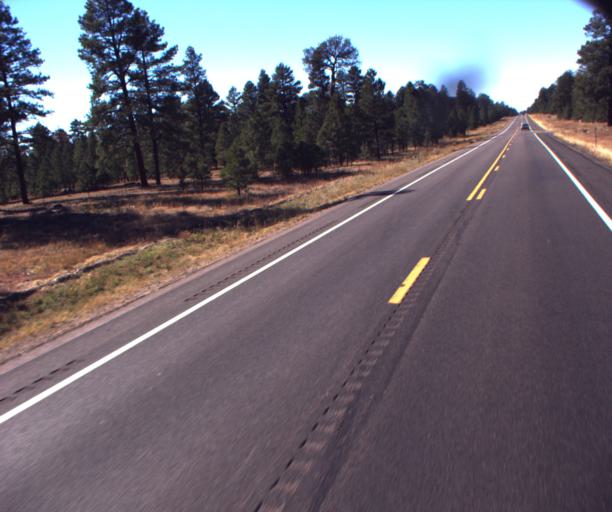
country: US
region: Arizona
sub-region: Apache County
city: Saint Michaels
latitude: 35.6865
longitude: -109.2422
